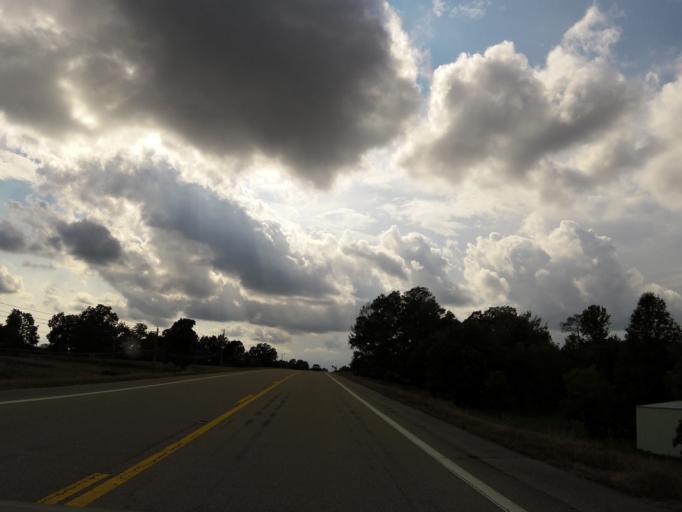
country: US
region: Mississippi
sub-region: Alcorn County
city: Corinth
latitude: 34.9817
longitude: -88.4984
